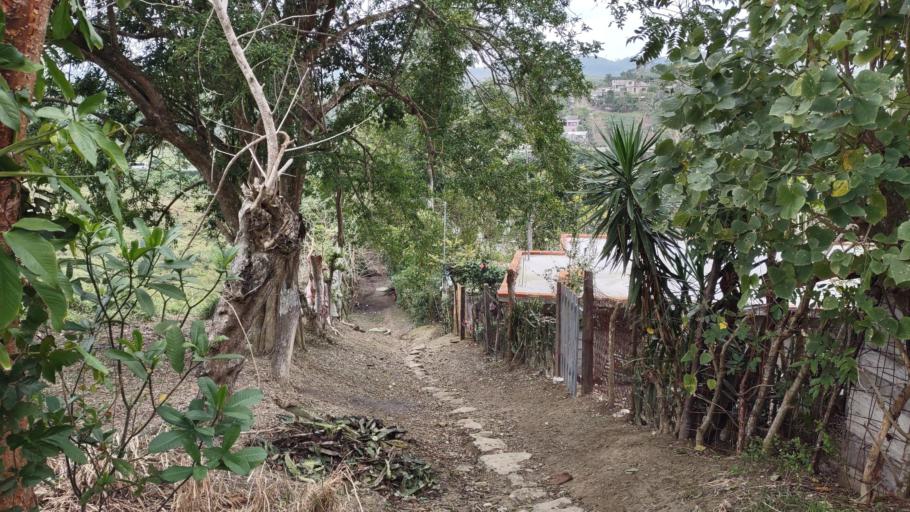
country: MX
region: Veracruz
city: Coatzintla
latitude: 20.4569
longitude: -97.4212
